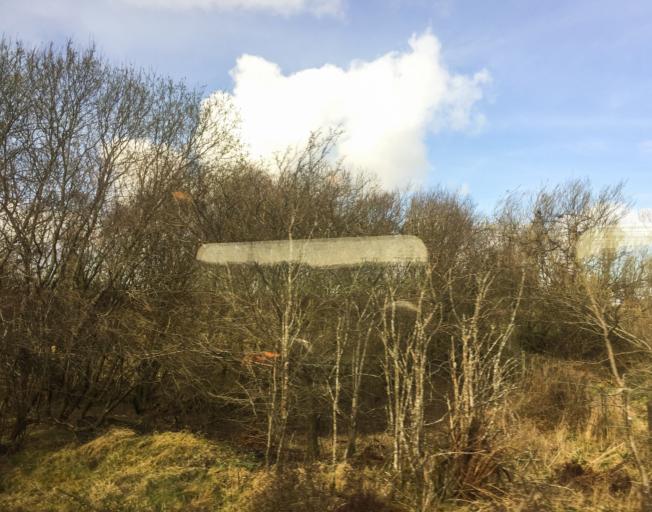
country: GB
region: Scotland
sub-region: North Lanarkshire
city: Glenboig
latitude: 55.8837
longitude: -4.0672
